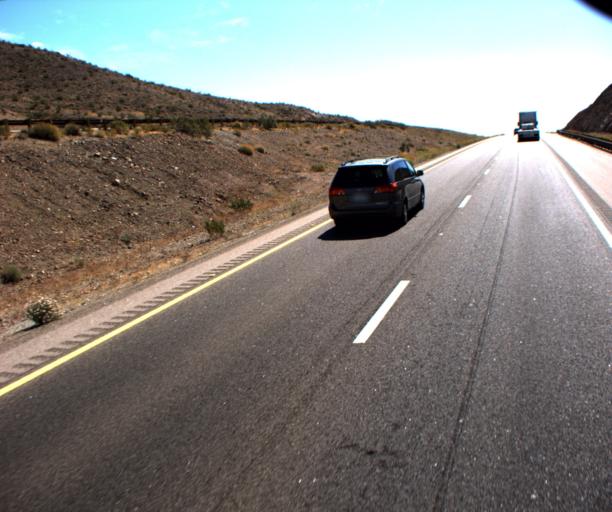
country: US
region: Nevada
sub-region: Clark County
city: Boulder City
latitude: 35.8478
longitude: -114.5853
